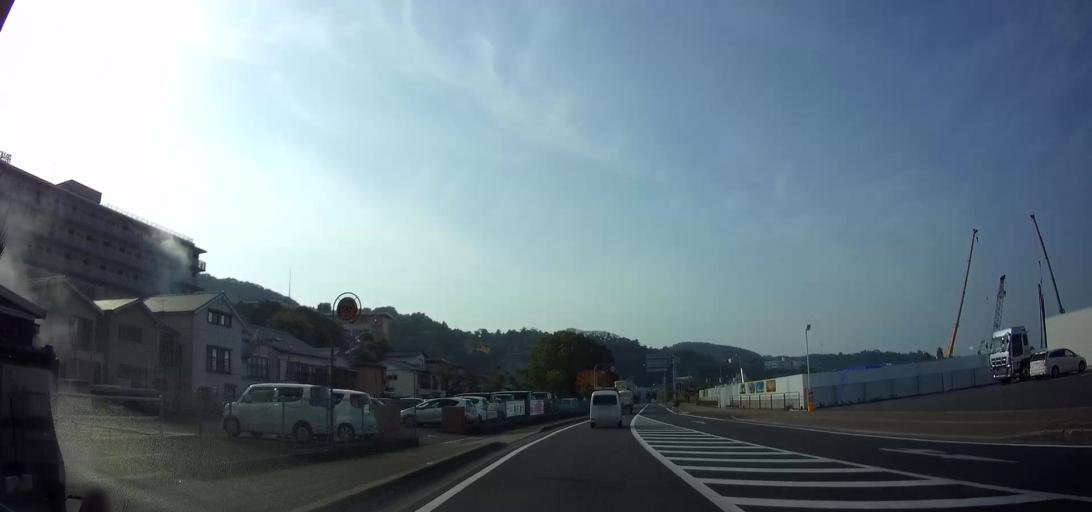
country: JP
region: Nagasaki
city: Shimabara
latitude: 32.7231
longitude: 130.2037
